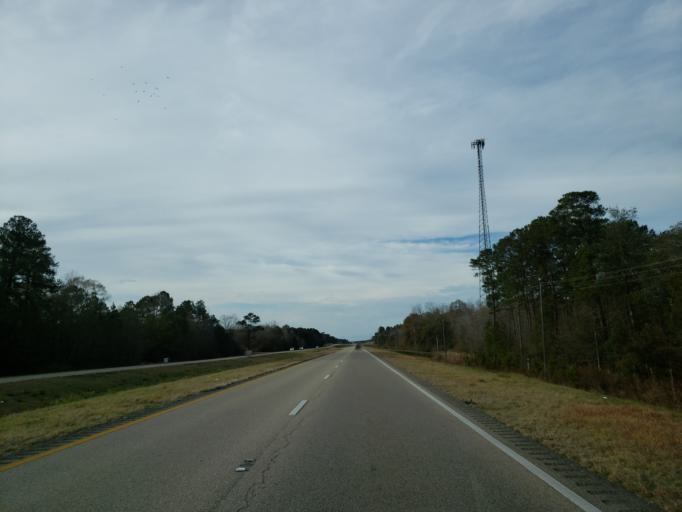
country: US
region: Mississippi
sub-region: Wayne County
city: Belmont
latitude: 31.6127
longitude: -88.5710
